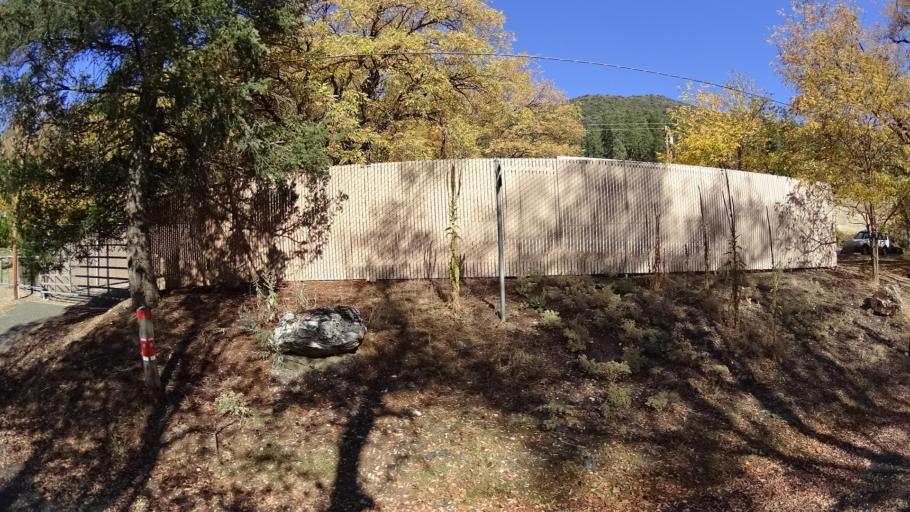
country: US
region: California
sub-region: Siskiyou County
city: Yreka
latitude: 41.7419
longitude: -122.9904
